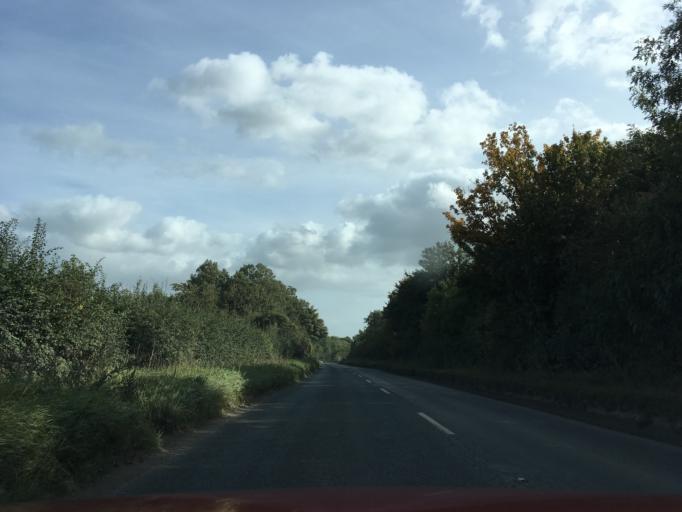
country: GB
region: England
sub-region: South Gloucestershire
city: Charfield
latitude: 51.6098
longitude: -2.4111
